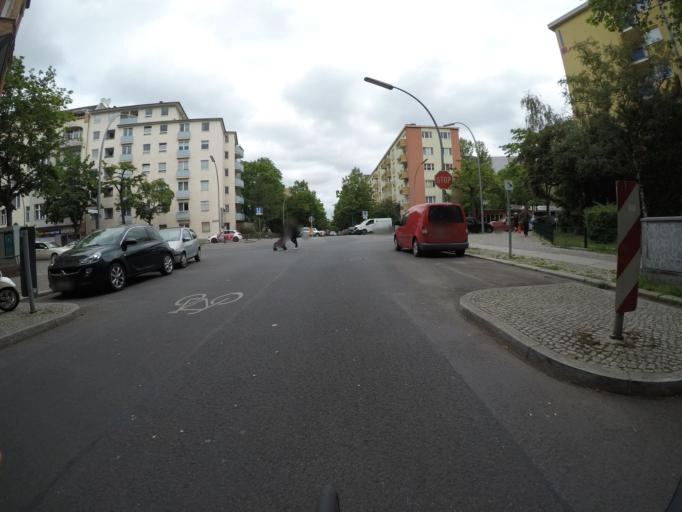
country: DE
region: Berlin
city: Berlin Schoeneberg
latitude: 52.4872
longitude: 13.3332
